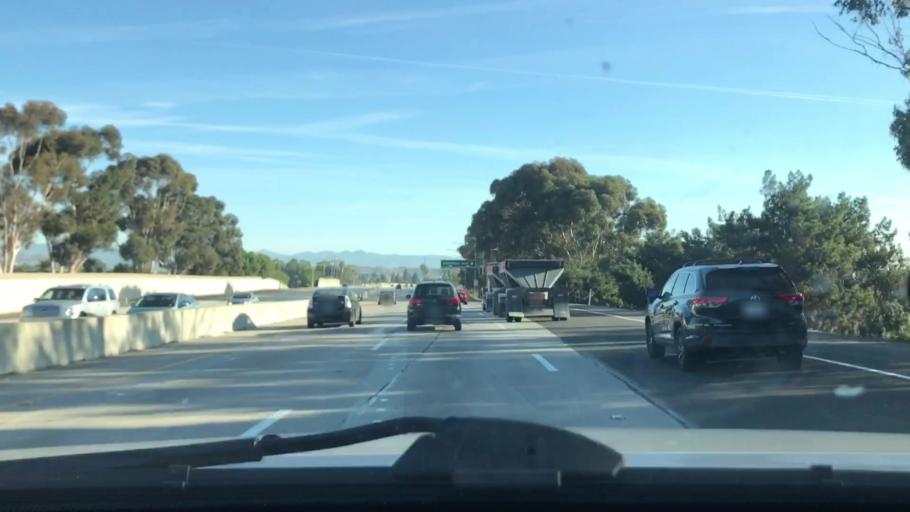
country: US
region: California
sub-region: Los Angeles County
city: Marina del Rey
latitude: 33.9821
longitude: -118.4181
